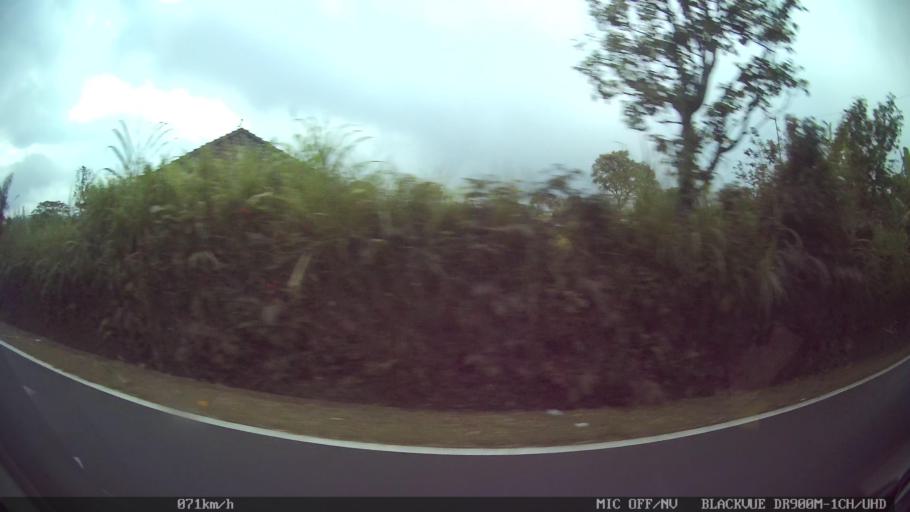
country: ID
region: Bali
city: Banjar Kedisan
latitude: -8.2760
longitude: 115.3277
